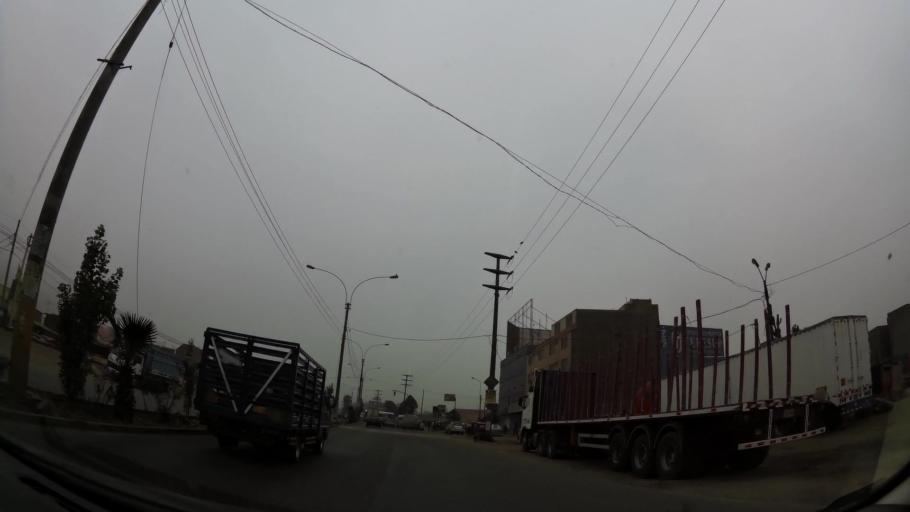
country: PE
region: Lima
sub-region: Lima
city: Santa Maria
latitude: -12.0051
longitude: -76.8451
